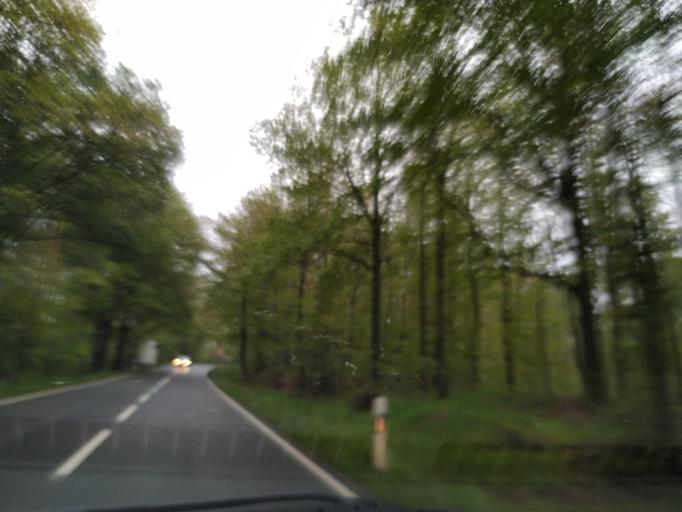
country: DE
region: Saxony
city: Hartmannsdorf
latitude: 50.7743
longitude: 12.4317
